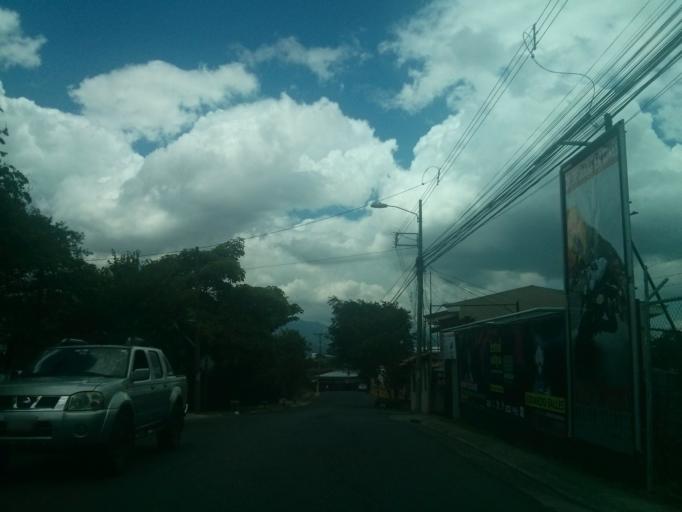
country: CR
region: San Jose
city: San Pedro
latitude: 9.9233
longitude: -84.0490
